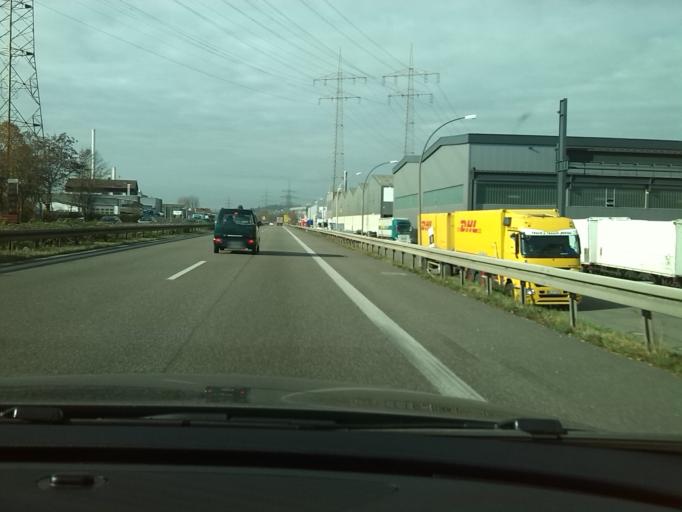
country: DE
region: Baden-Wuerttemberg
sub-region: Regierungsbezirk Stuttgart
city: Deizisau
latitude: 48.7136
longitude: 9.4009
